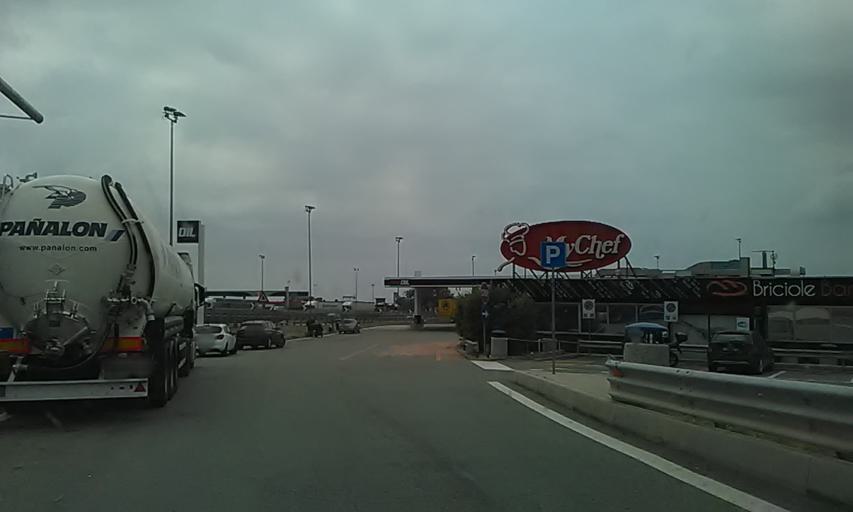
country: IT
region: Liguria
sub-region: Provincia di Genova
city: Mele
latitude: 44.4558
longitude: 8.7443
